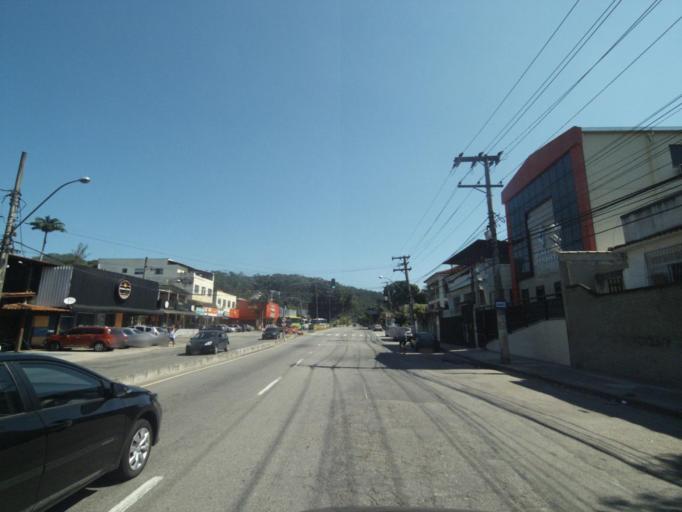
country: BR
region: Rio de Janeiro
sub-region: Niteroi
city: Niteroi
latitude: -22.8978
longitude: -43.0401
